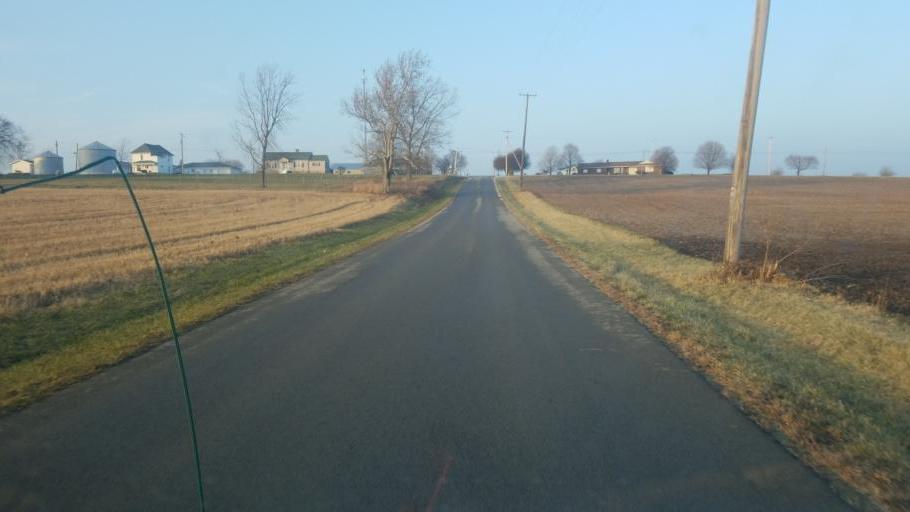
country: US
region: Ohio
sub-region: Wyandot County
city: Carey
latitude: 40.9603
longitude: -83.4292
